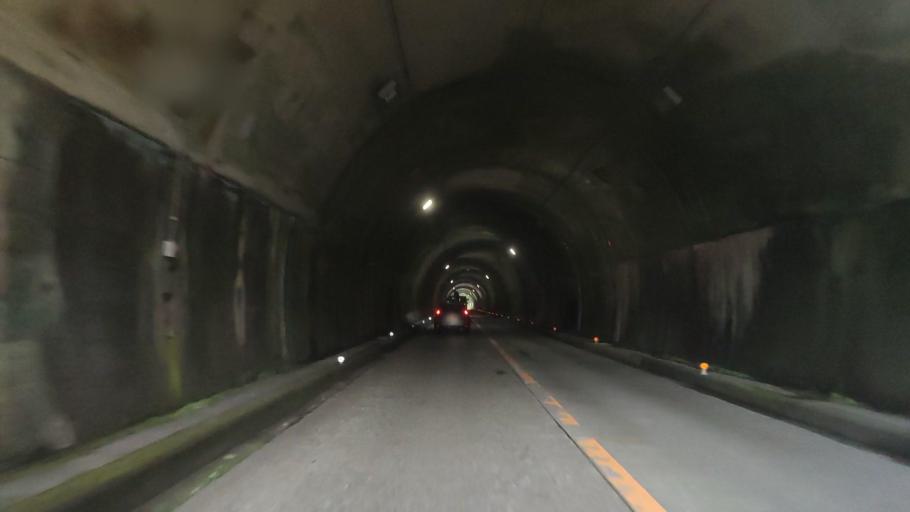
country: JP
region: Wakayama
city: Shingu
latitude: 33.8167
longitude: 135.8563
